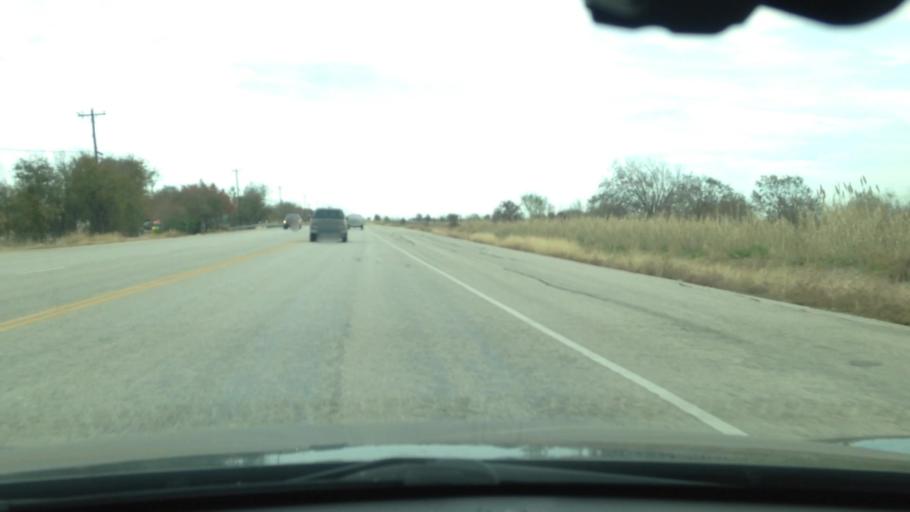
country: US
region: Texas
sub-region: Caldwell County
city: Martindale
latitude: 29.9062
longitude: -97.8632
